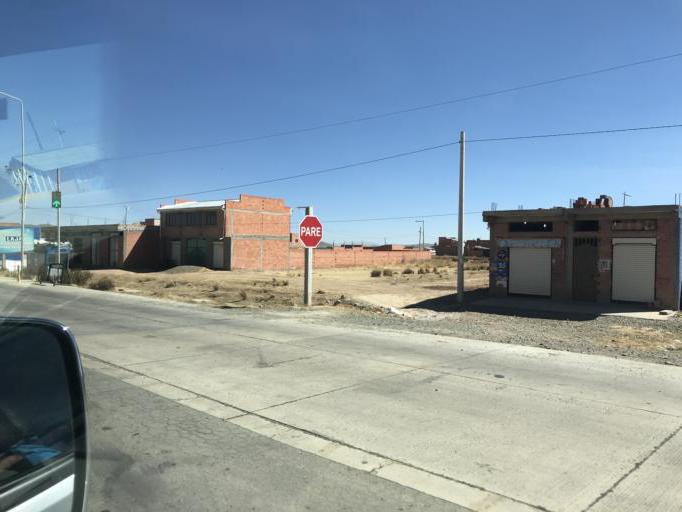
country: BO
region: La Paz
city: La Paz
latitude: -16.5312
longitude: -68.3861
